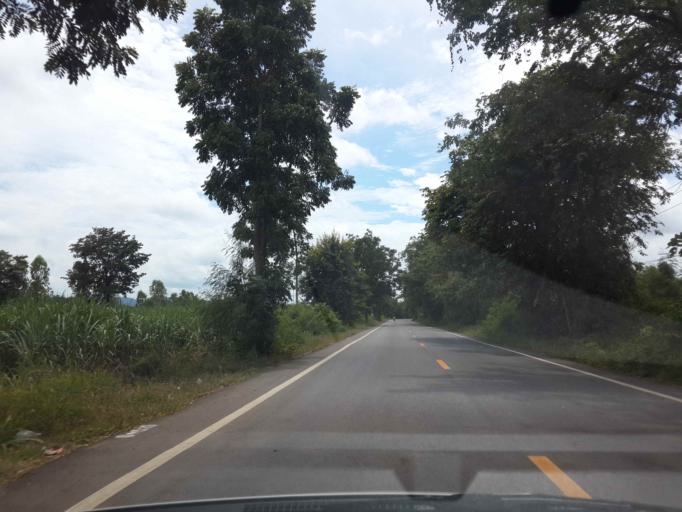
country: TH
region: Ratchaburi
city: Pak Tho
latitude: 13.4128
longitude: 99.6715
